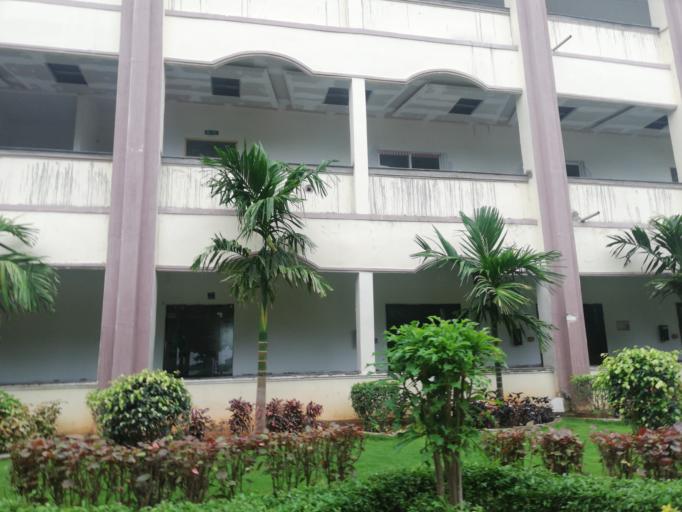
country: IN
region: Telangana
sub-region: Rangareddi
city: Quthbullapur
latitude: 17.5944
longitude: 78.4411
